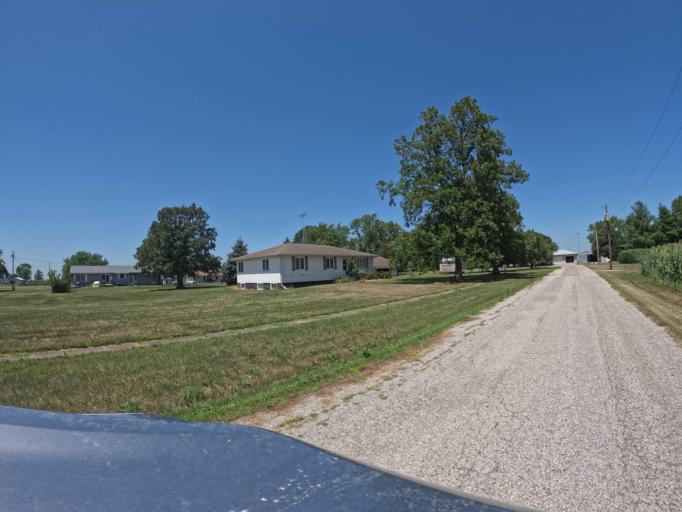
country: US
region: Iowa
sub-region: Keokuk County
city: Sigourney
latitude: 41.4562
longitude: -92.3322
